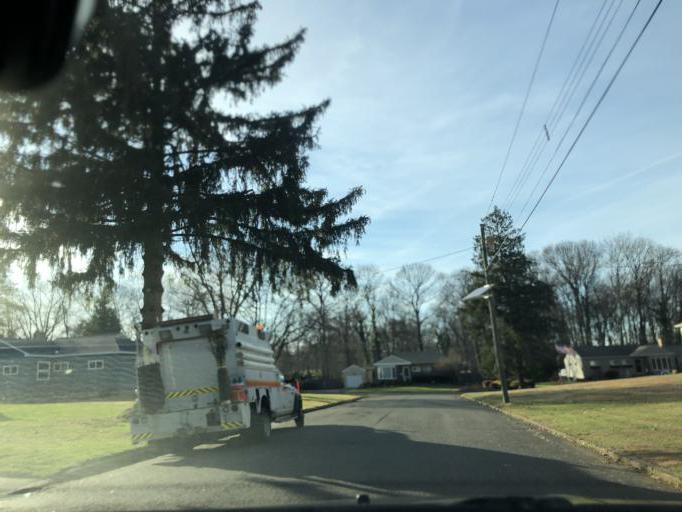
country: US
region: New Jersey
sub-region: Burlington County
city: Moorestown-Lenola
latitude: 39.9604
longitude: -74.9718
